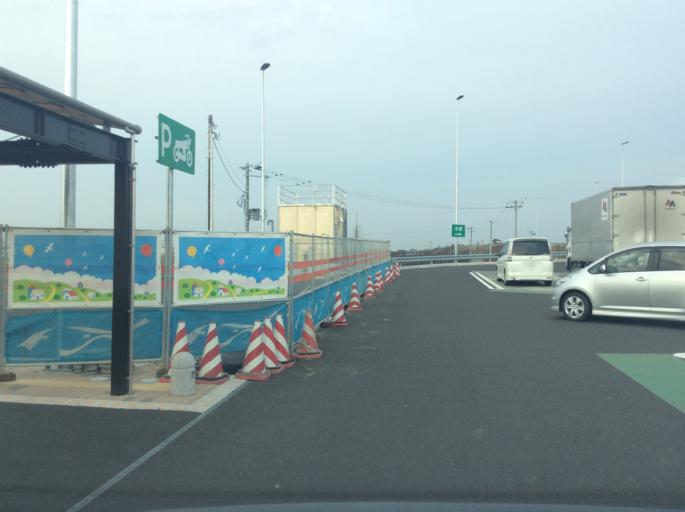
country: JP
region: Miyagi
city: Watari
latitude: 38.0395
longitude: 140.8922
